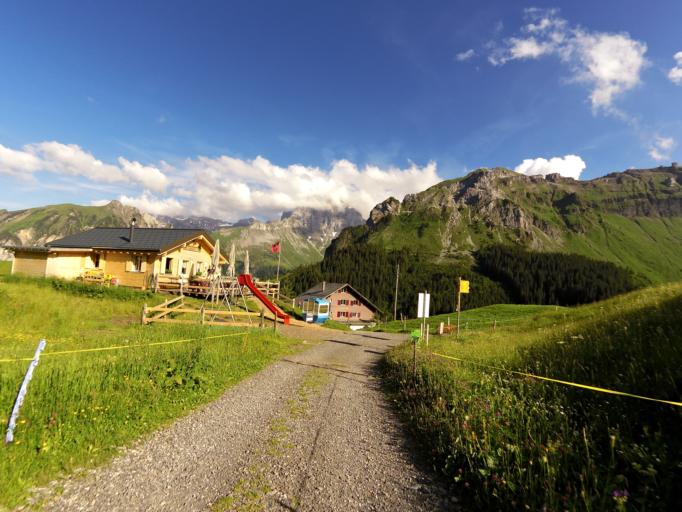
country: CH
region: Nidwalden
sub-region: Nidwalden
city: Emmetten
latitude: 46.9006
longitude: 8.4996
